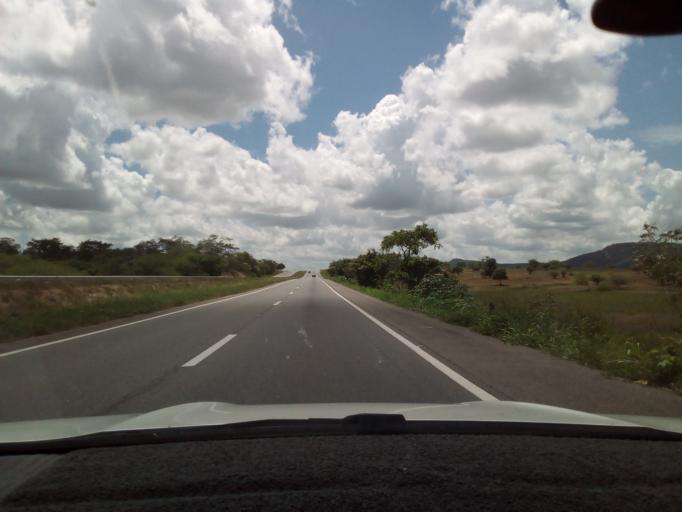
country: BR
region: Paraiba
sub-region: Gurinhem
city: Gurinhem
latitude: -7.1930
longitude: -35.4785
